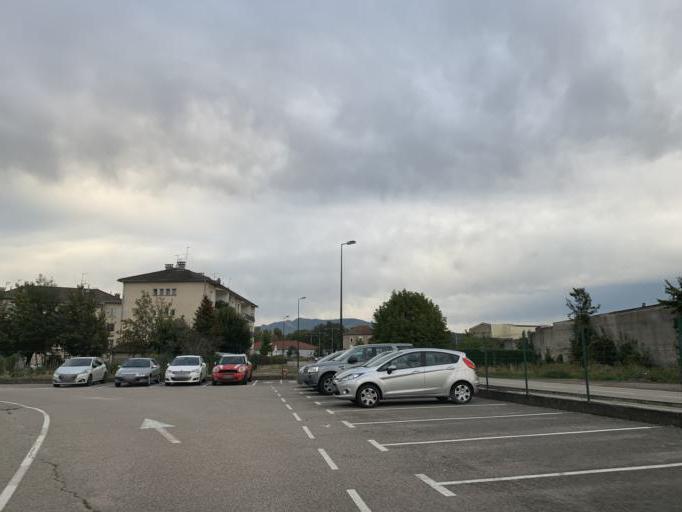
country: FR
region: Rhone-Alpes
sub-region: Departement de l'Ain
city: Belley
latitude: 45.7568
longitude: 5.6962
